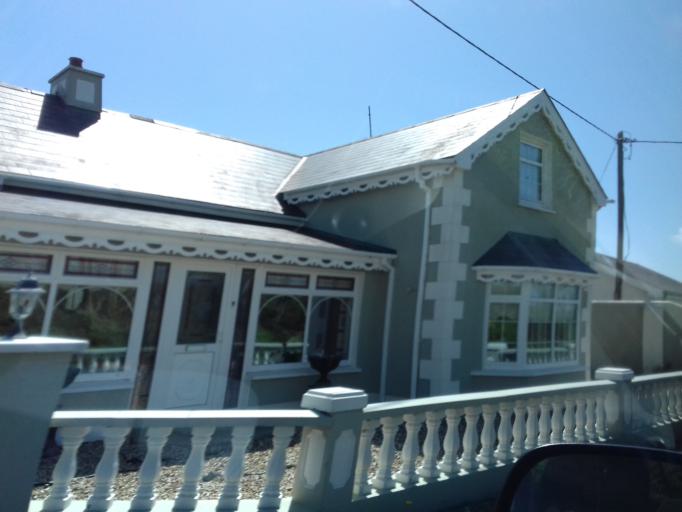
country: IE
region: Munster
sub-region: Waterford
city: Dunmore East
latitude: 52.1947
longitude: -6.8547
